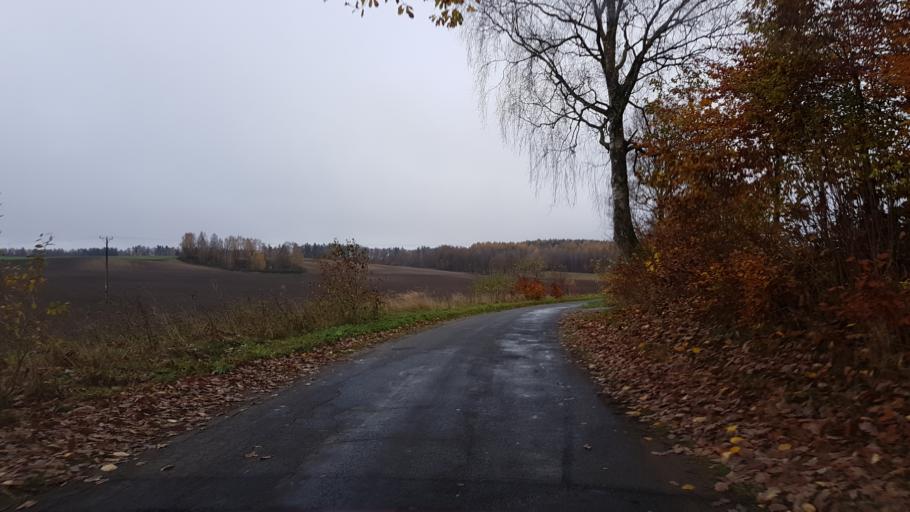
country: PL
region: West Pomeranian Voivodeship
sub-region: Powiat koszalinski
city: Polanow
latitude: 54.0877
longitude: 16.5951
